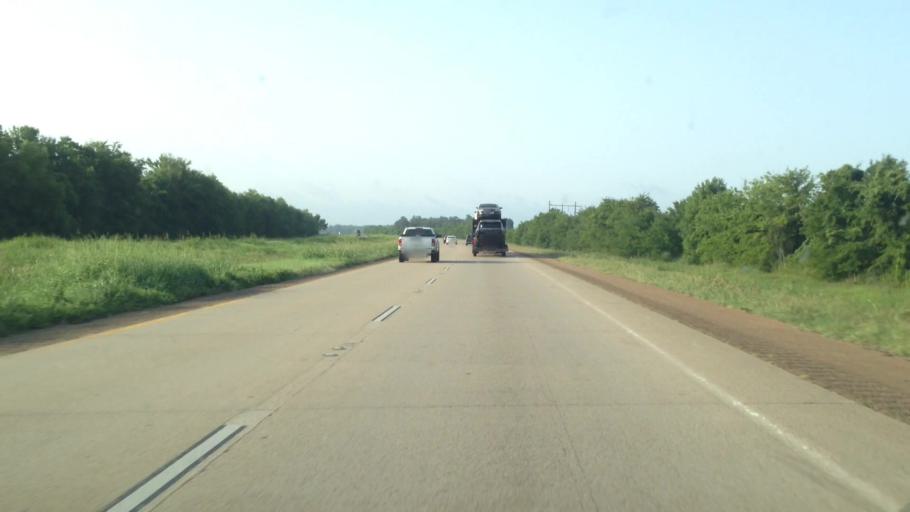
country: US
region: Louisiana
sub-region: Rapides Parish
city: Woodworth
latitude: 31.1942
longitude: -92.4742
